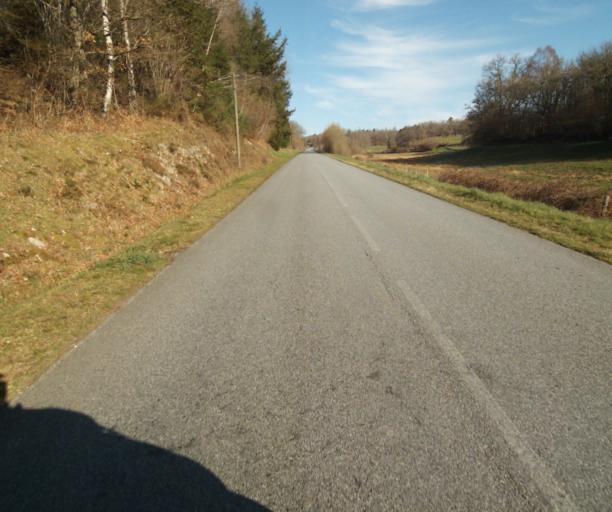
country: FR
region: Limousin
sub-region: Departement de la Correze
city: Correze
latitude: 45.3137
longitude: 1.8862
